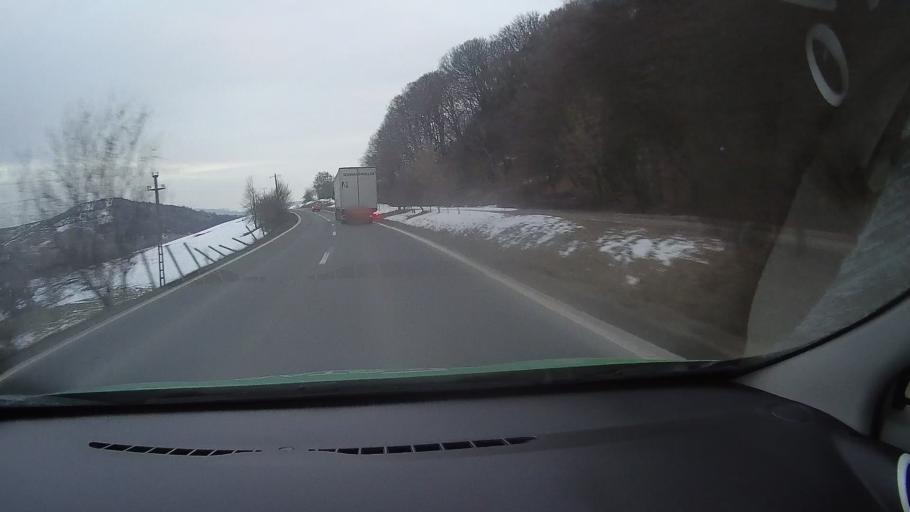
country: RO
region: Harghita
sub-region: Municipiul Odorheiu Secuiesc
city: Odorheiu Secuiesc
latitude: 46.3287
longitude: 25.2761
